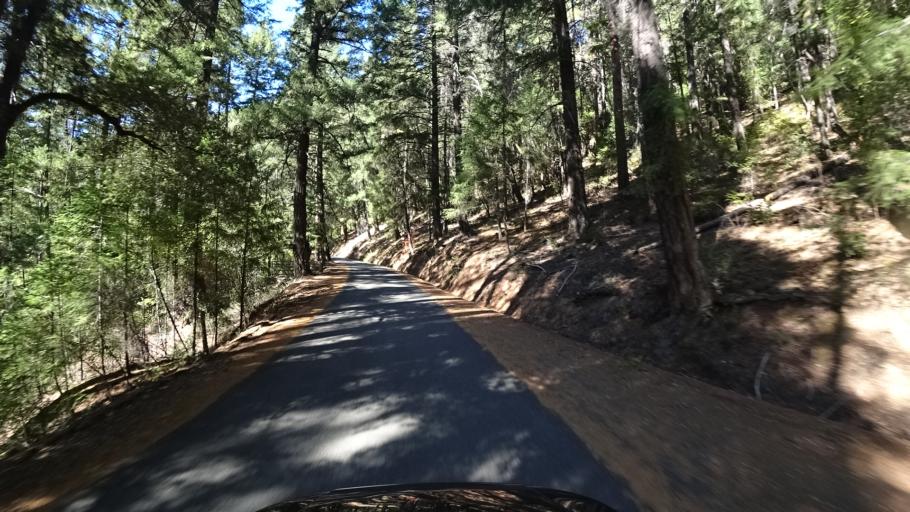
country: US
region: California
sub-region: Siskiyou County
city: Happy Camp
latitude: 41.2991
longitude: -123.1194
